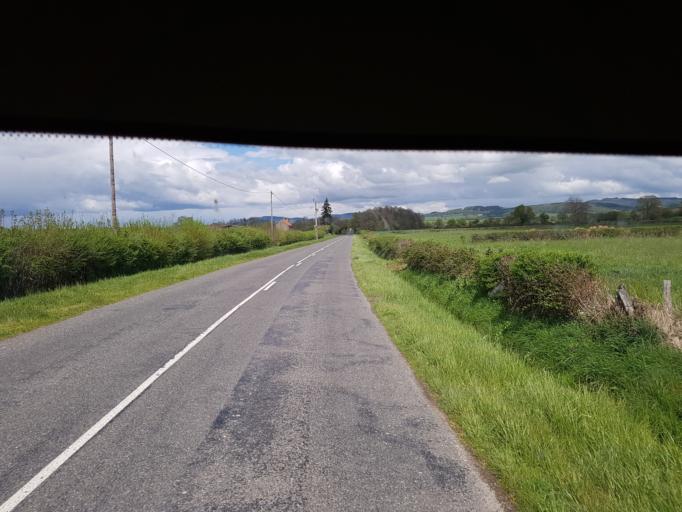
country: FR
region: Bourgogne
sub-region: Departement de Saone-et-Loire
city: Etang-sur-Arroux
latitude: 46.8191
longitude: 4.1671
